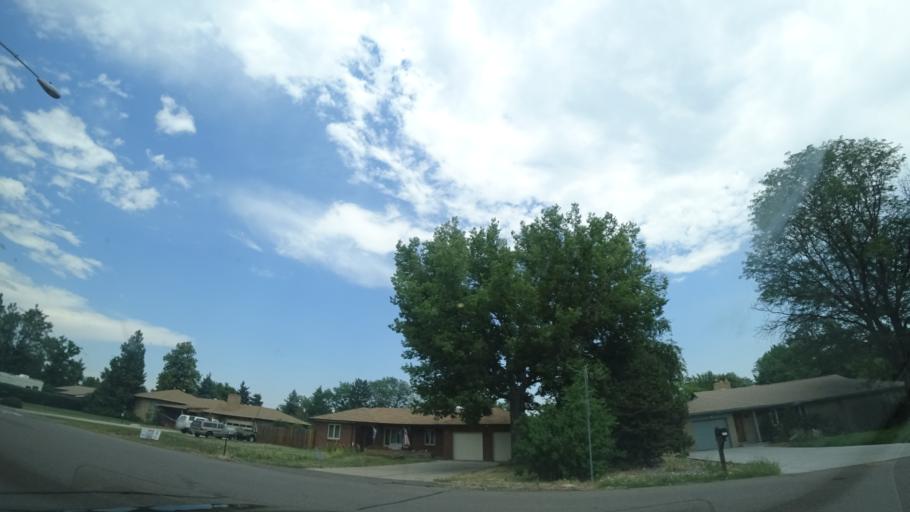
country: US
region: Colorado
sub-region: Jefferson County
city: Lakewood
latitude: 39.7197
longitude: -105.0910
